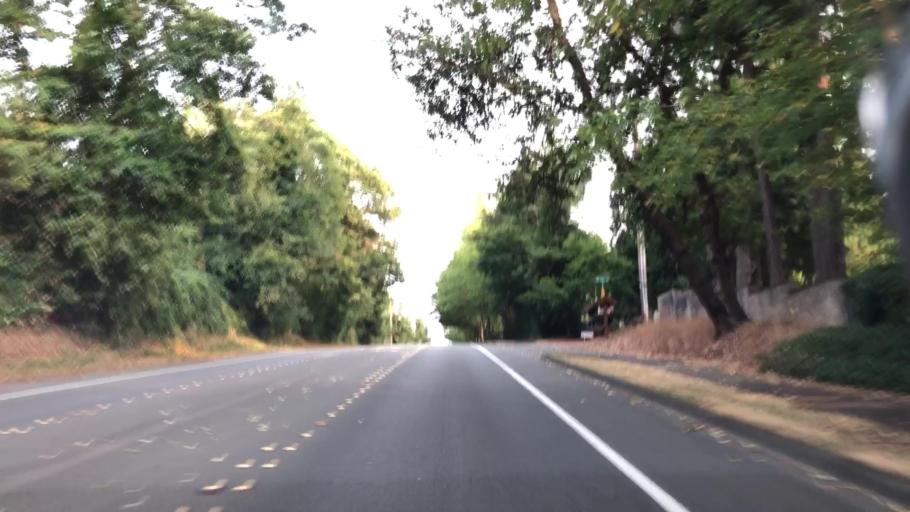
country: US
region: Washington
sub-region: King County
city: Mercer Island
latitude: 47.5659
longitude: -122.2258
